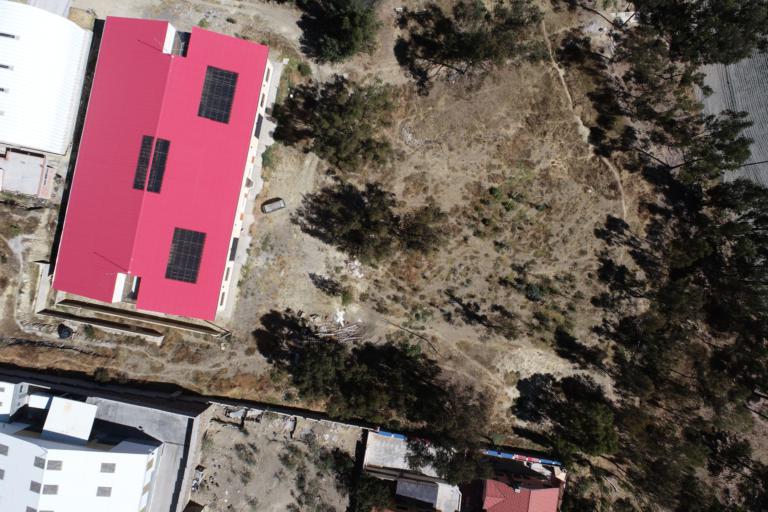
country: BO
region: La Paz
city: La Paz
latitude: -16.5377
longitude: -68.0586
